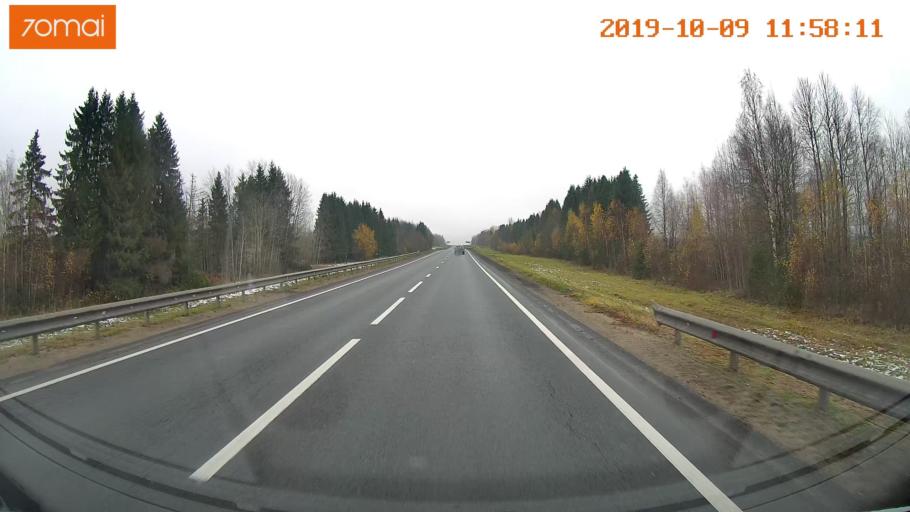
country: RU
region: Vologda
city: Gryazovets
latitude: 58.7216
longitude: 40.2962
